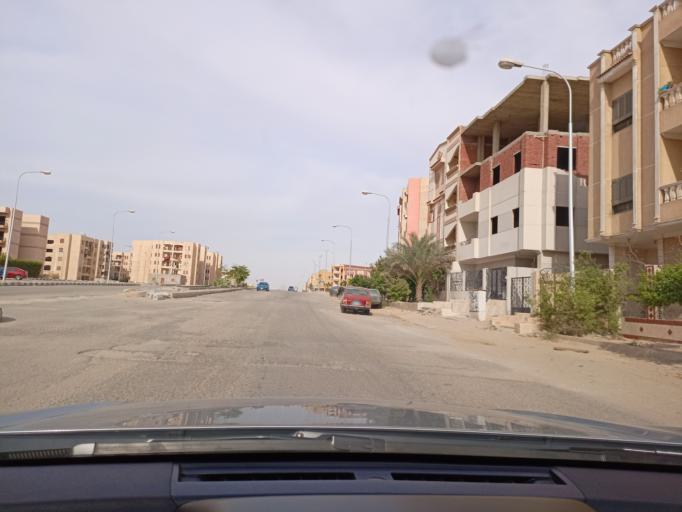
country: EG
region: Muhafazat al Qalyubiyah
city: Al Khankah
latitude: 30.2602
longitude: 31.4903
